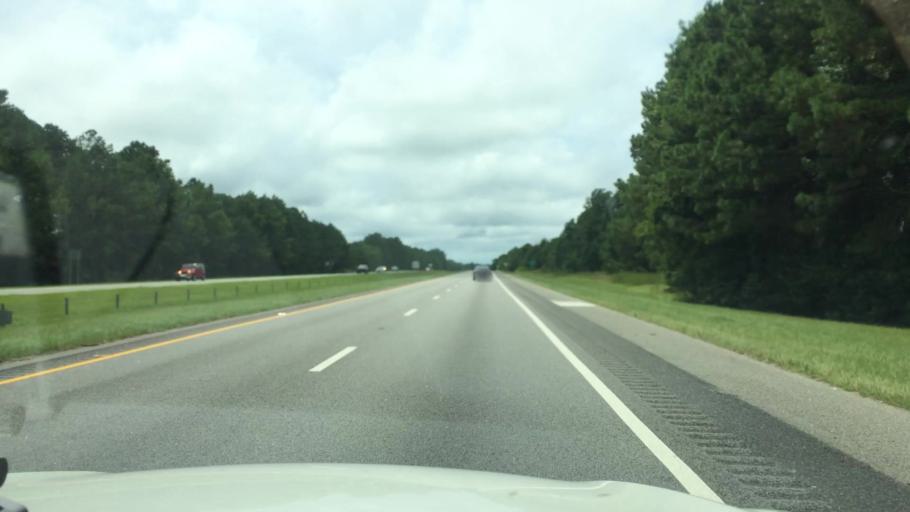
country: US
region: South Carolina
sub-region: Florence County
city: Timmonsville
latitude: 34.2045
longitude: -79.8792
